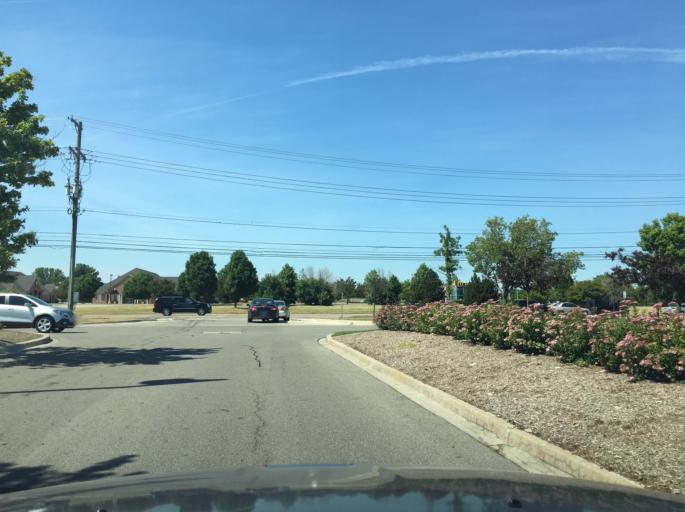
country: US
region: Michigan
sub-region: Macomb County
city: Clinton
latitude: 42.6273
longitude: -82.9422
